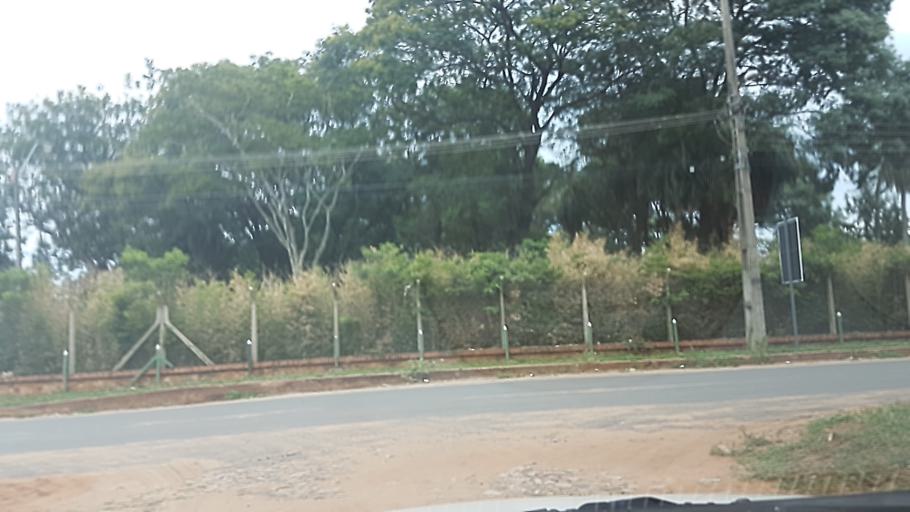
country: PY
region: Central
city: Colonia Mariano Roque Alonso
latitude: -25.2124
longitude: -57.5258
